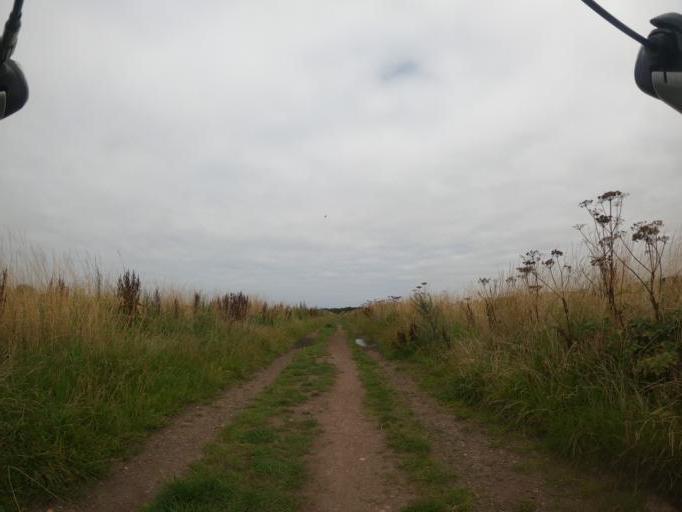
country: GB
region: Scotland
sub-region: East Lothian
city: Musselburgh
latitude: 55.9400
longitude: -3.0904
